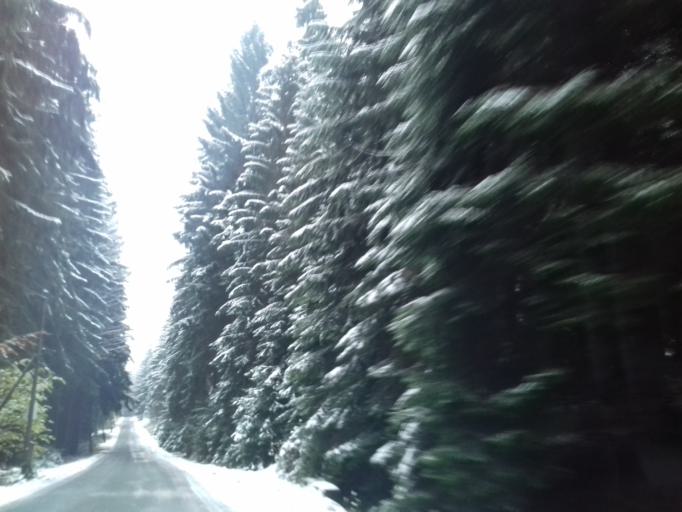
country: CZ
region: Plzensky
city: Postrekov
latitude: 49.4406
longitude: 12.7856
